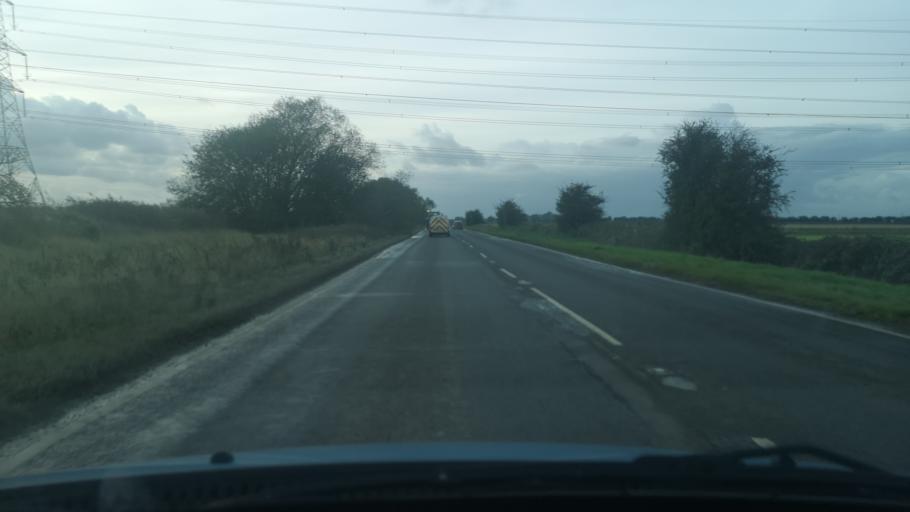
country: GB
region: England
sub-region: North Lincolnshire
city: Gunness
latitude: 53.5772
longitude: -0.7593
